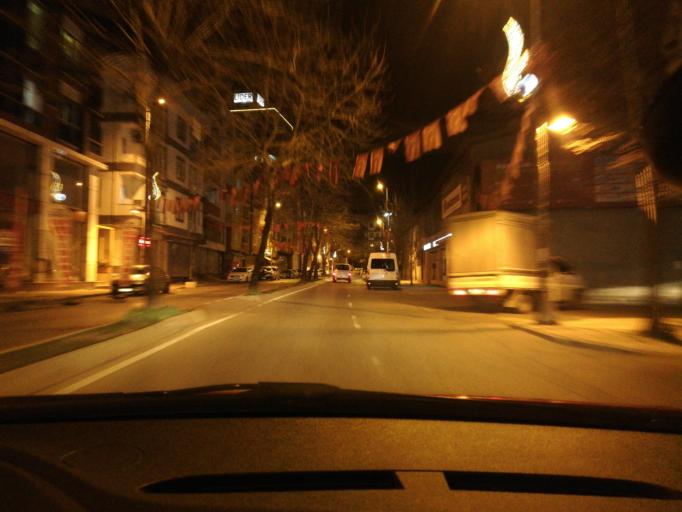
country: TR
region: Istanbul
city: Sisli
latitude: 41.0829
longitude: 28.9734
